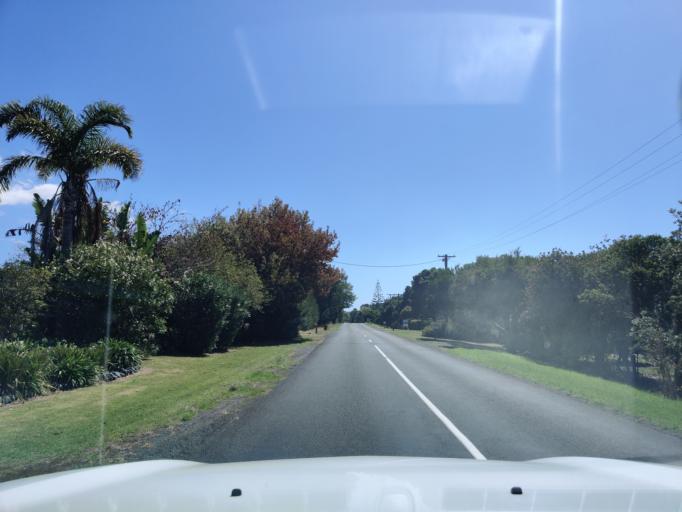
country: NZ
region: Waikato
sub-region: Thames-Coromandel District
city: Thames
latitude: -37.0491
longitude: 175.2998
